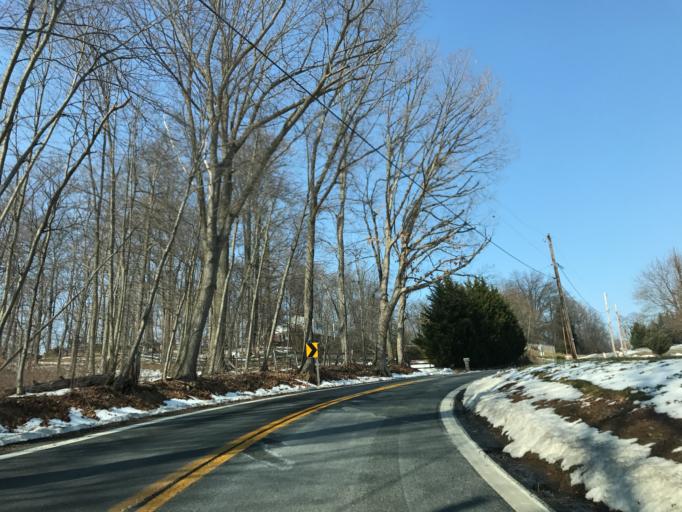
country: US
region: Pennsylvania
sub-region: York County
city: Susquehanna Trails
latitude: 39.7042
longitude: -76.4089
